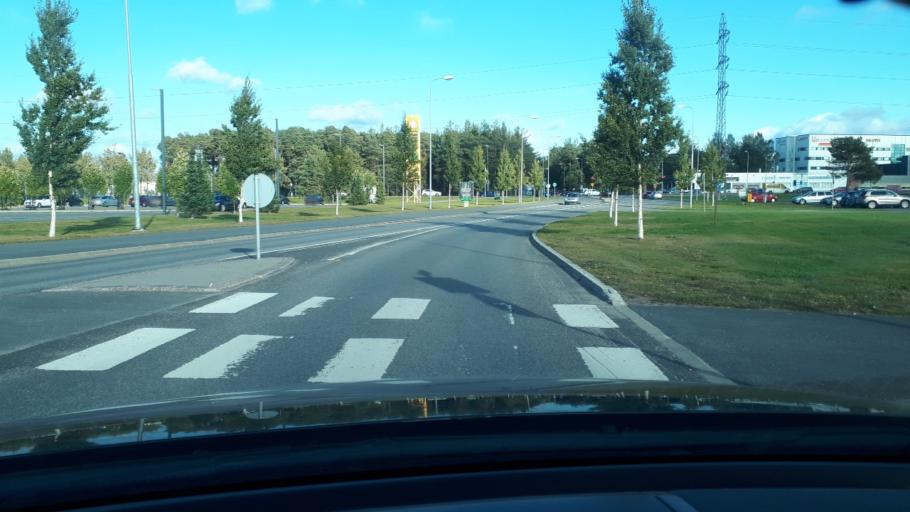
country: FI
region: Northern Ostrobothnia
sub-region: Oulu
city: Oulu
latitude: 64.9922
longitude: 25.4615
